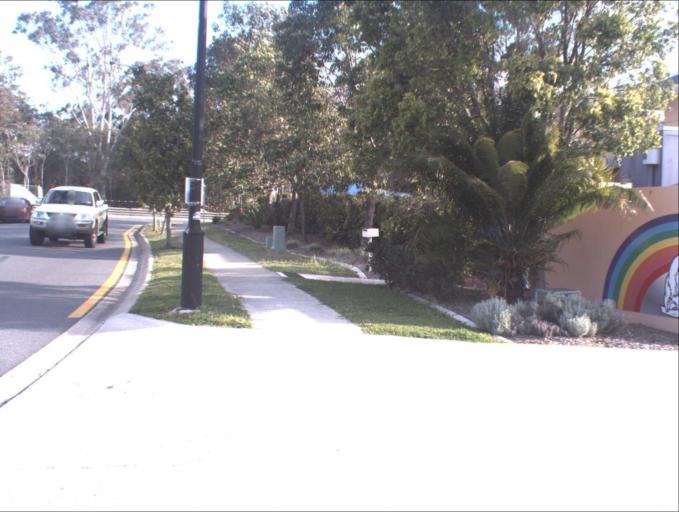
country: AU
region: Queensland
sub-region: Logan
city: Logan Reserve
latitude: -27.6994
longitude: 153.0983
